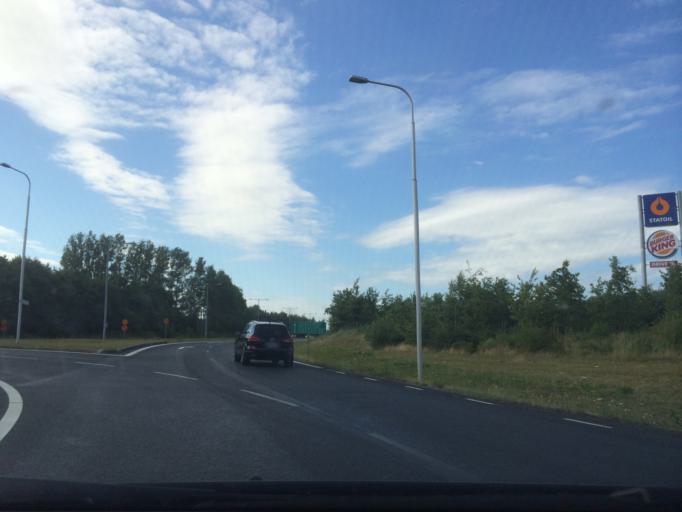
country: SE
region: Skane
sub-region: Malmo
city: Bunkeflostrand
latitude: 55.5564
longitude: 12.9545
